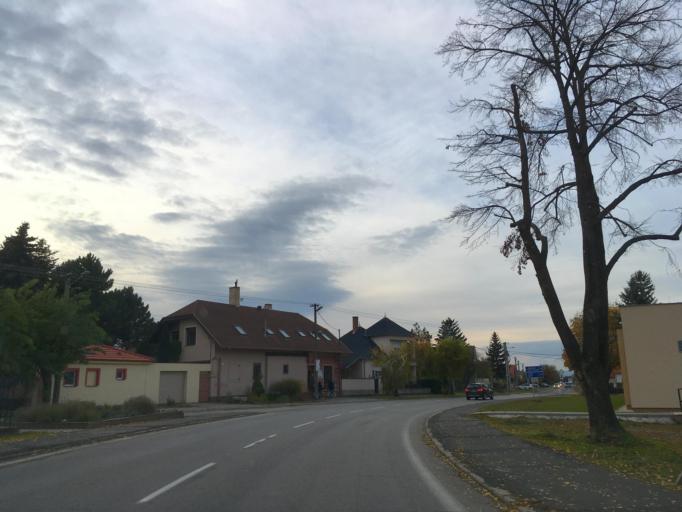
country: SK
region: Trnavsky
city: Samorin
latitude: 48.0993
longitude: 17.3536
